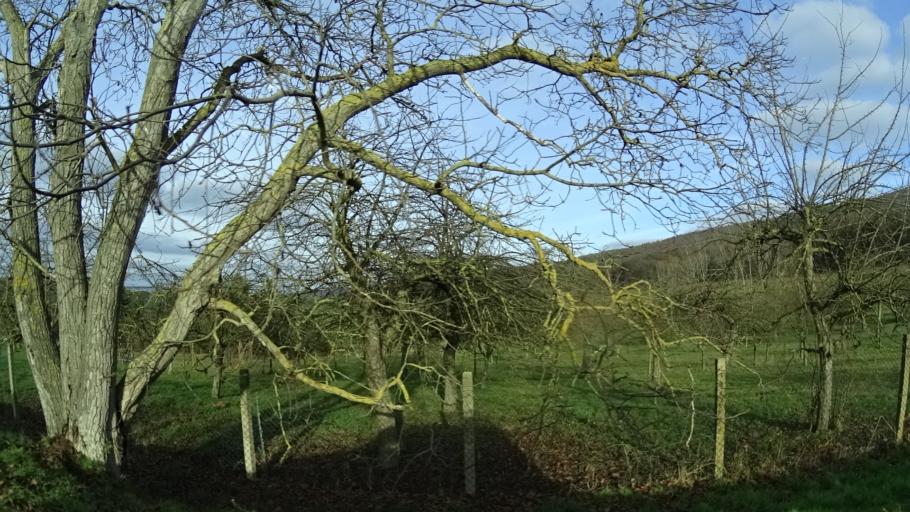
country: DE
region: Bavaria
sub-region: Regierungsbezirk Unterfranken
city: Grossheubach
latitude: 49.7439
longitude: 9.2462
